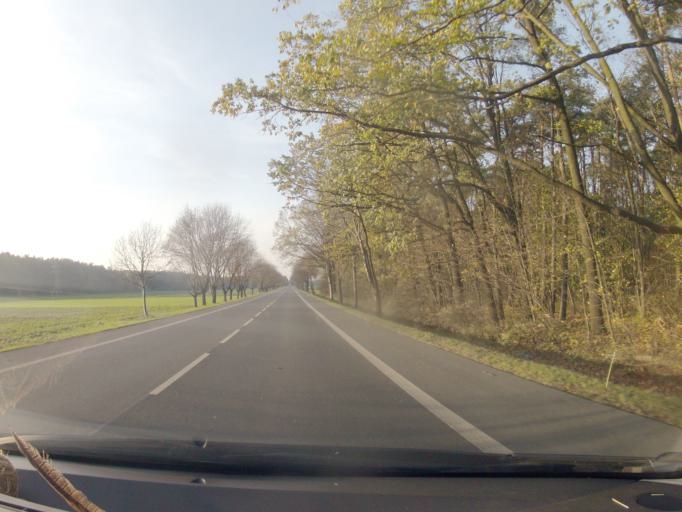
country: PL
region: Opole Voivodeship
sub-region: Powiat strzelecki
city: Strzelce Opolskie
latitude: 50.5376
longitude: 18.2504
